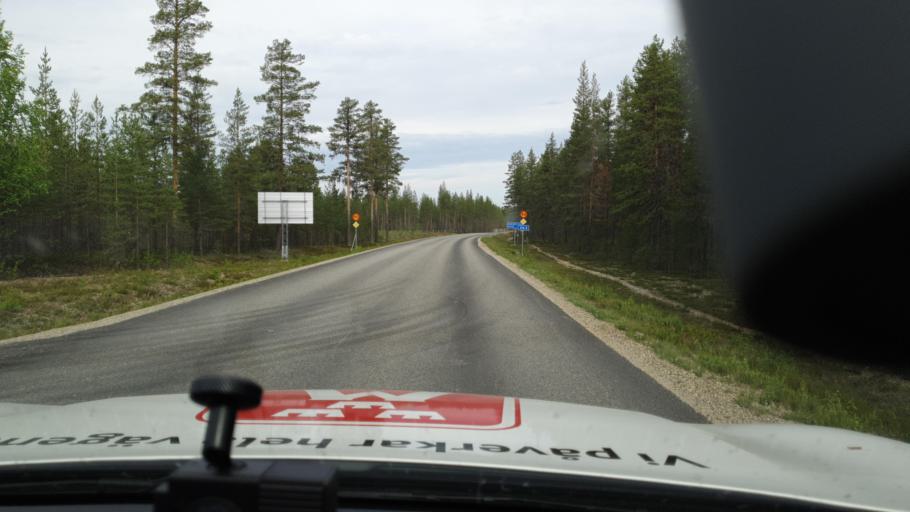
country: SE
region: Vaesterbotten
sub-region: Lycksele Kommun
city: Lycksele
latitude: 64.8266
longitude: 18.7955
